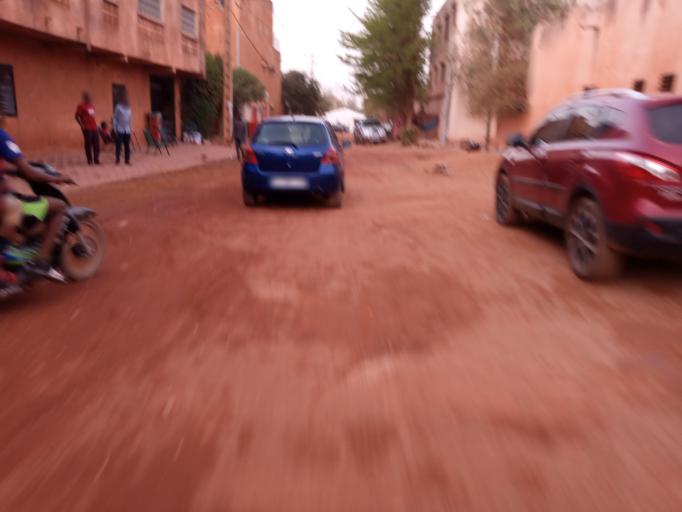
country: ML
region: Bamako
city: Bamako
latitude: 12.5820
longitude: -7.9526
